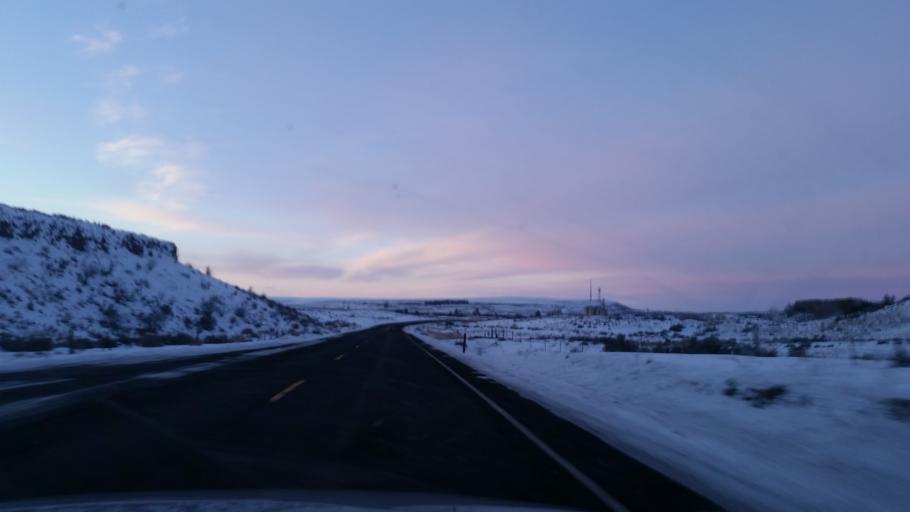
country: US
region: Washington
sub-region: Spokane County
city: Medical Lake
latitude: 47.2896
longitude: -117.9680
